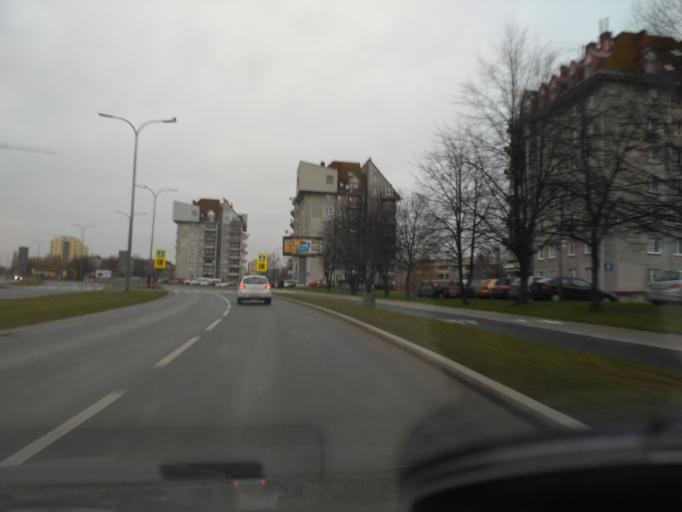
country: PL
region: Lublin Voivodeship
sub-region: Powiat lubelski
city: Lublin
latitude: 51.2567
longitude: 22.5541
